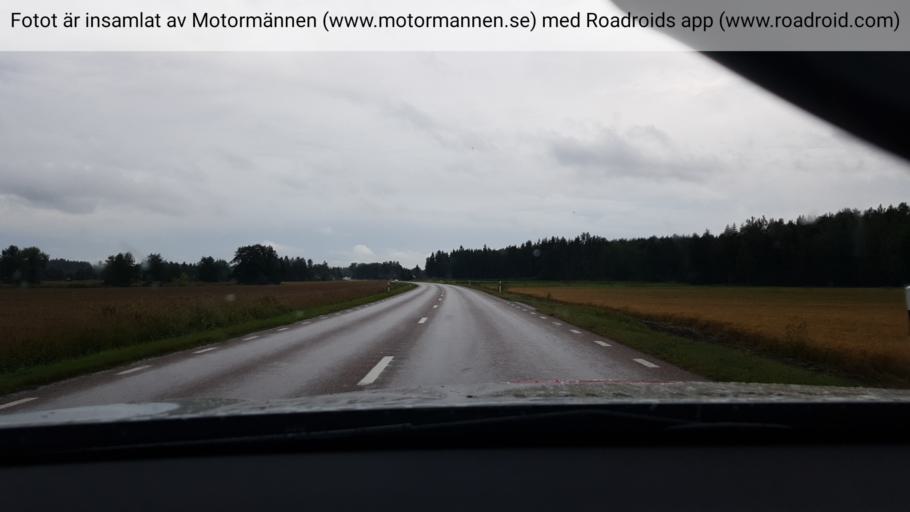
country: SE
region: Uppsala
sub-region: Tierps Kommun
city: Karlholmsbruk
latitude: 60.4504
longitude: 17.7713
